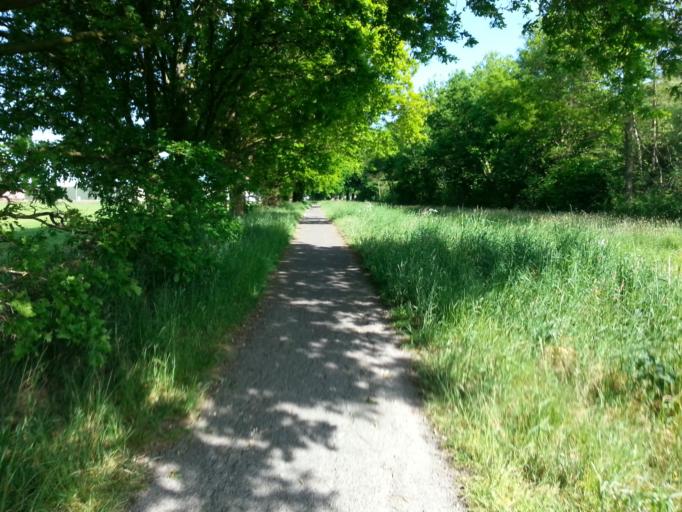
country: NL
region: Gelderland
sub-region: Berkelland
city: Neede
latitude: 52.1265
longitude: 6.6278
